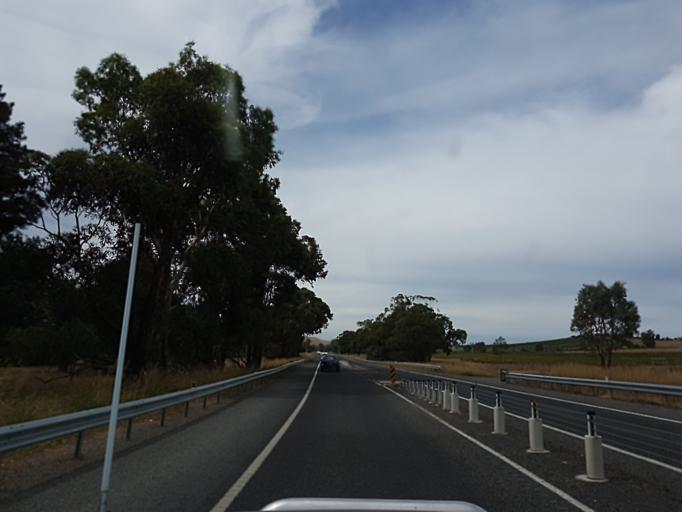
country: AU
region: Victoria
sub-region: Murrindindi
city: Alexandra
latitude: -37.2092
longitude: 145.4553
